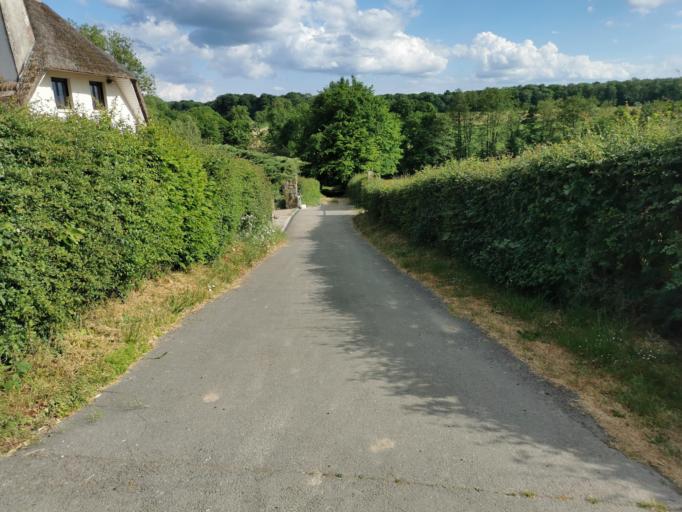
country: FR
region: Nord-Pas-de-Calais
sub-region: Departement du Nord
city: Jeumont
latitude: 50.2182
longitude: 4.1090
